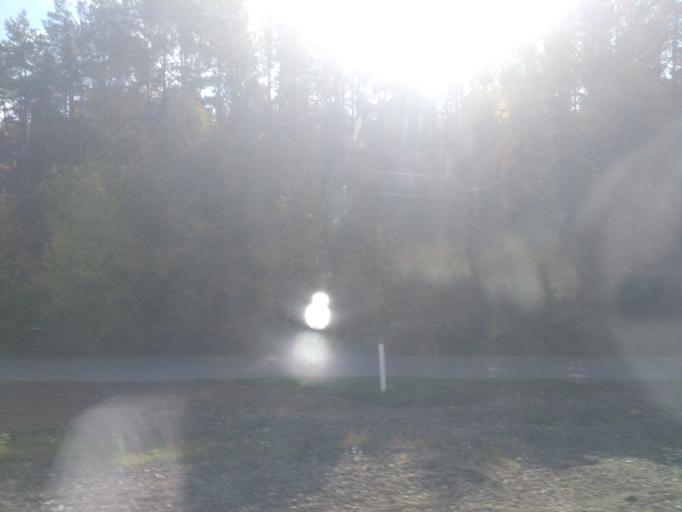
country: RU
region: Tatarstan
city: Aysha
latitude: 55.8417
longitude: 48.5790
